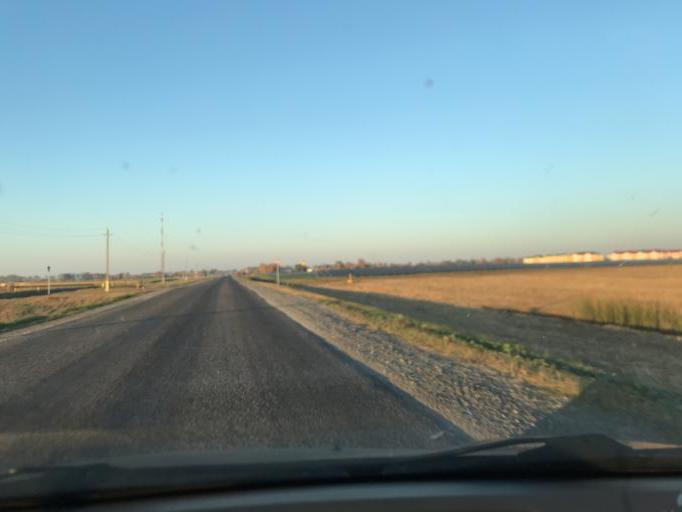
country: BY
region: Gomel
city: Brahin
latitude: 51.7808
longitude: 30.2521
